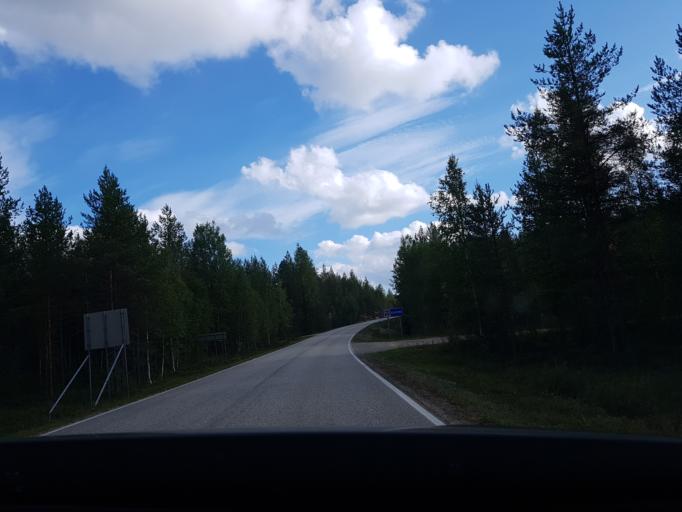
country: FI
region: Kainuu
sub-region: Kehys-Kainuu
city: Kuhmo
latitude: 64.6260
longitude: 29.6966
